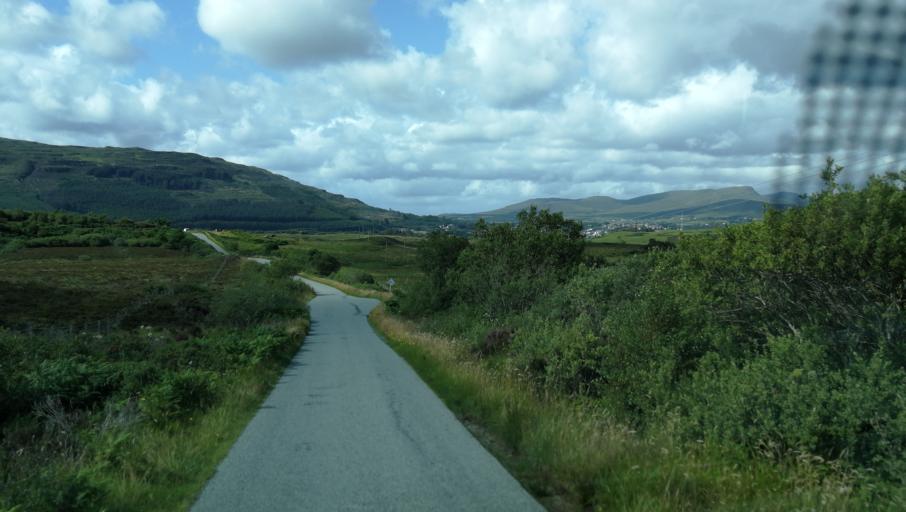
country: GB
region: Scotland
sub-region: Highland
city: Portree
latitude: 57.3814
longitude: -6.1731
